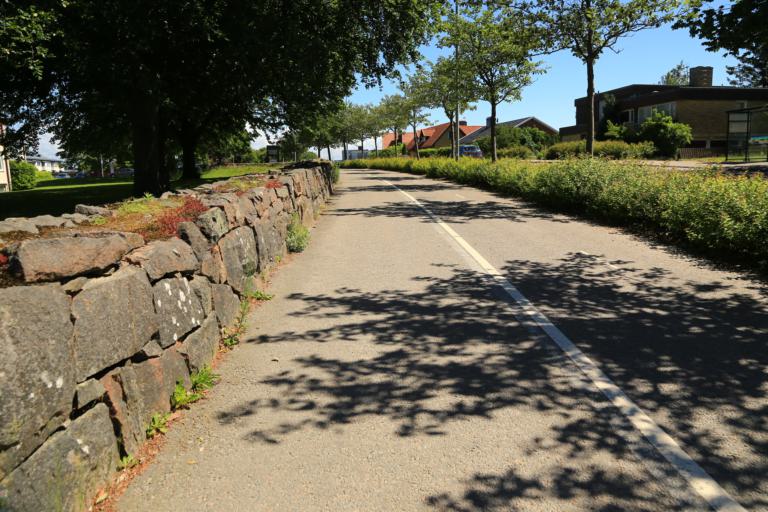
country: SE
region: Halland
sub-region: Varbergs Kommun
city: Varberg
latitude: 57.1028
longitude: 12.2637
